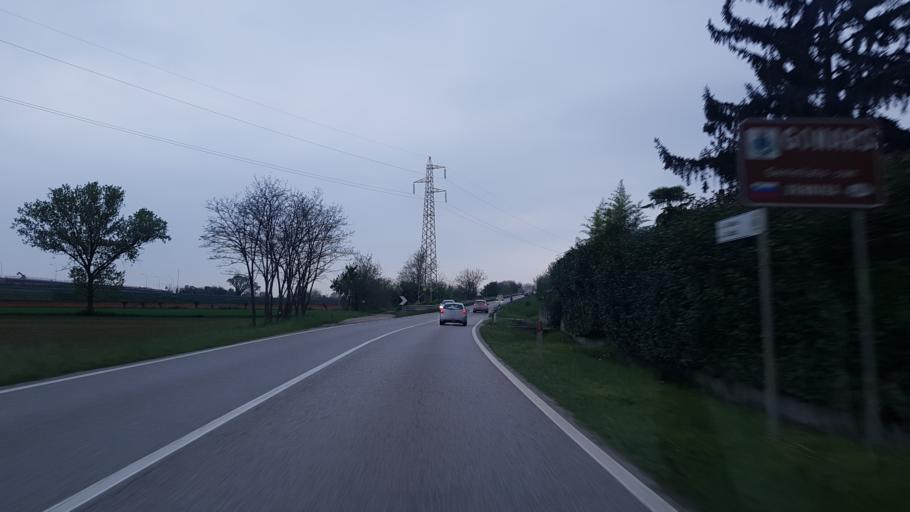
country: IT
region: Friuli Venezia Giulia
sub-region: Provincia di Udine
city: Bagnaria Arsa
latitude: 45.8993
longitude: 13.2913
